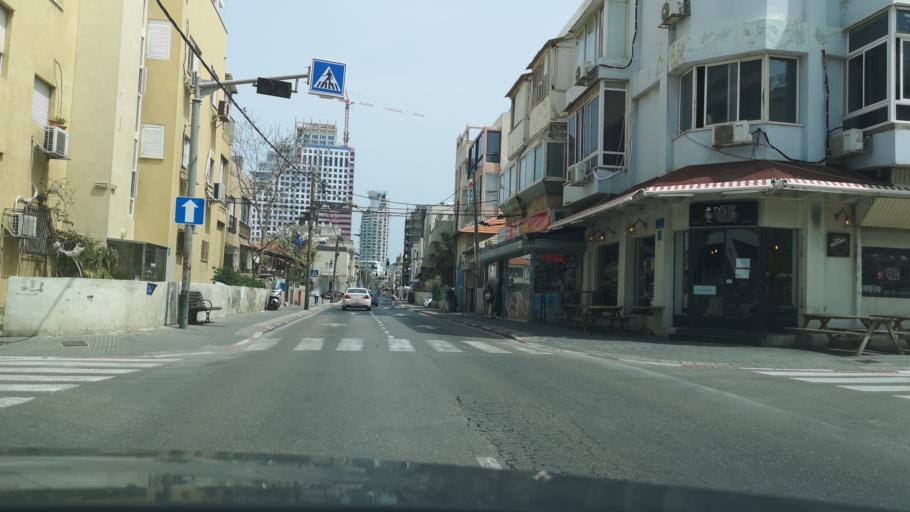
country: IL
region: Tel Aviv
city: Tel Aviv
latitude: 32.0704
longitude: 34.7649
